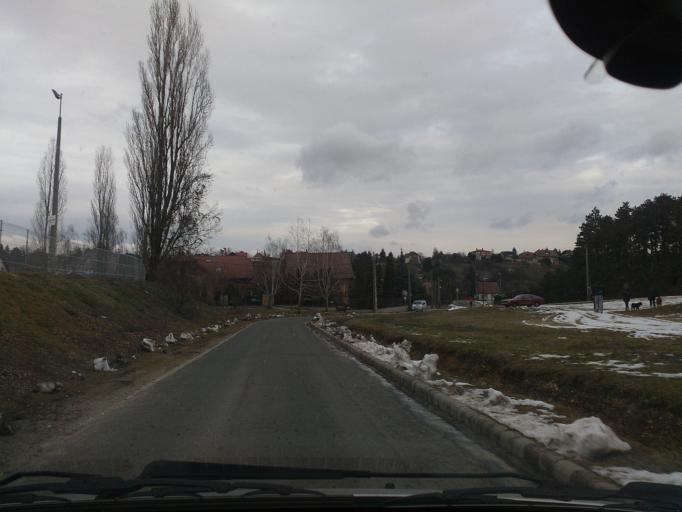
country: HU
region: Pest
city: Pilisszentivan
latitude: 47.6127
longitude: 18.8854
